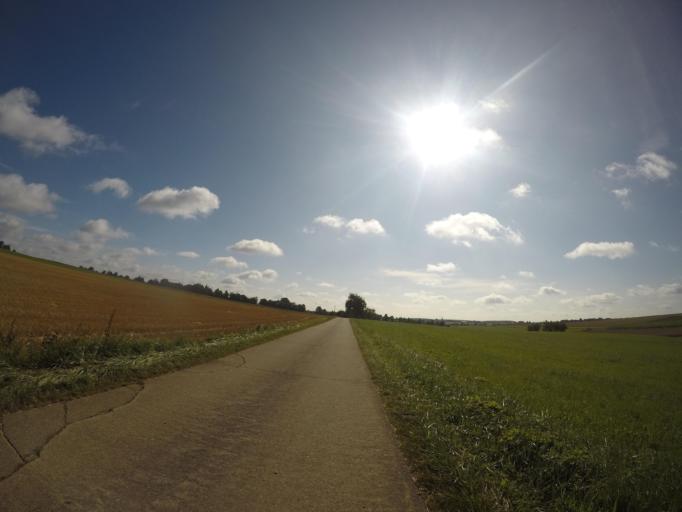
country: DE
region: Baden-Wuerttemberg
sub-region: Tuebingen Region
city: Mehrstetten
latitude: 48.3955
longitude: 9.6317
